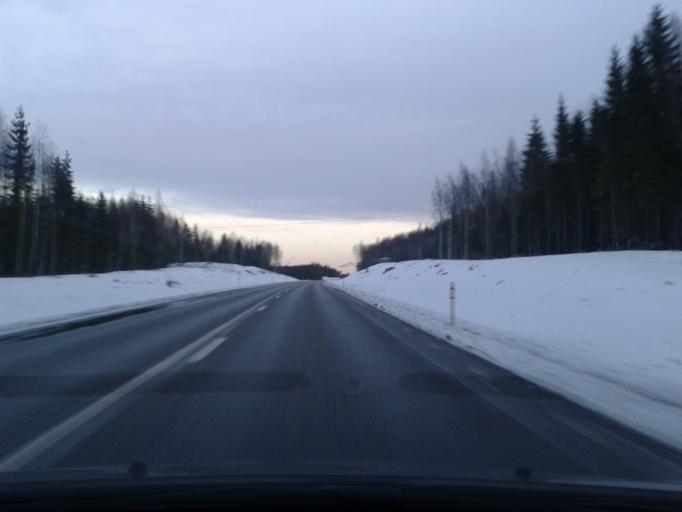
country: SE
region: Vaesternorrland
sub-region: Kramfors Kommun
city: Bollstabruk
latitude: 63.0595
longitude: 17.6043
